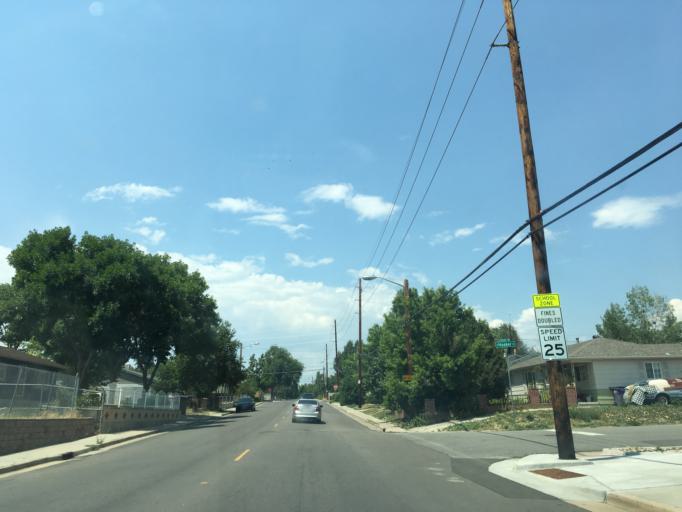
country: US
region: Colorado
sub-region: Arapahoe County
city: Sheridan
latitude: 39.6968
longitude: -105.0282
